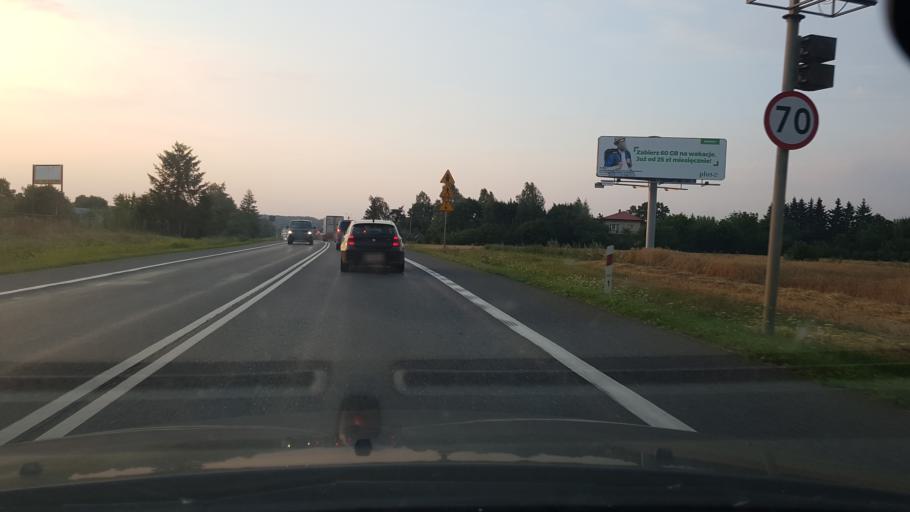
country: PL
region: Masovian Voivodeship
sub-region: Powiat mlawski
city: Mlawa
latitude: 53.1109
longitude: 20.4005
